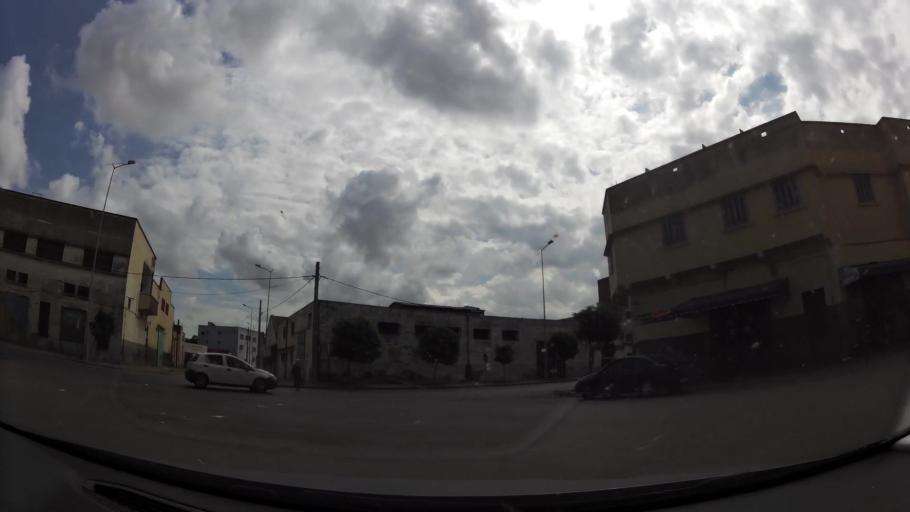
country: MA
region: Gharb-Chrarda-Beni Hssen
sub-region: Kenitra Province
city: Kenitra
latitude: 34.2662
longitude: -6.5720
